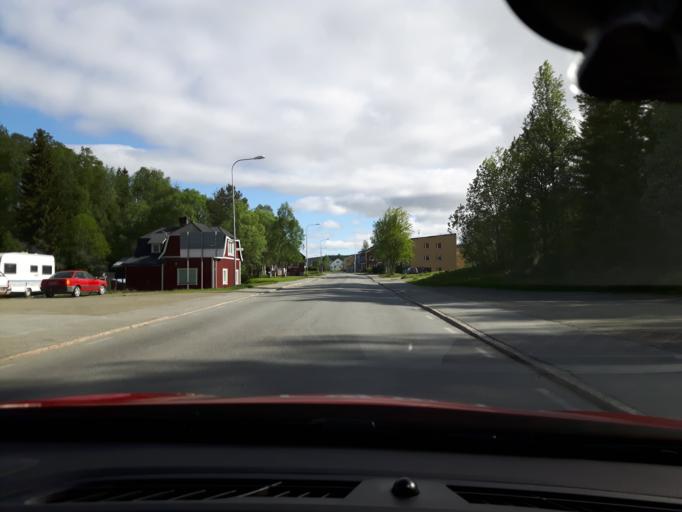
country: NO
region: Nord-Trondelag
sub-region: Lierne
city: Sandvika
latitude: 64.5003
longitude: 14.1428
